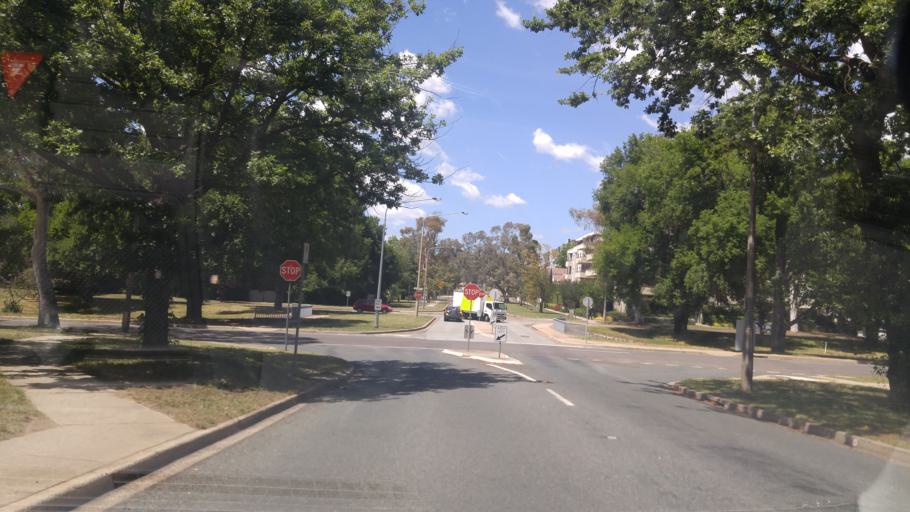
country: AU
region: Australian Capital Territory
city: Forrest
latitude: -35.3088
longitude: 149.1352
